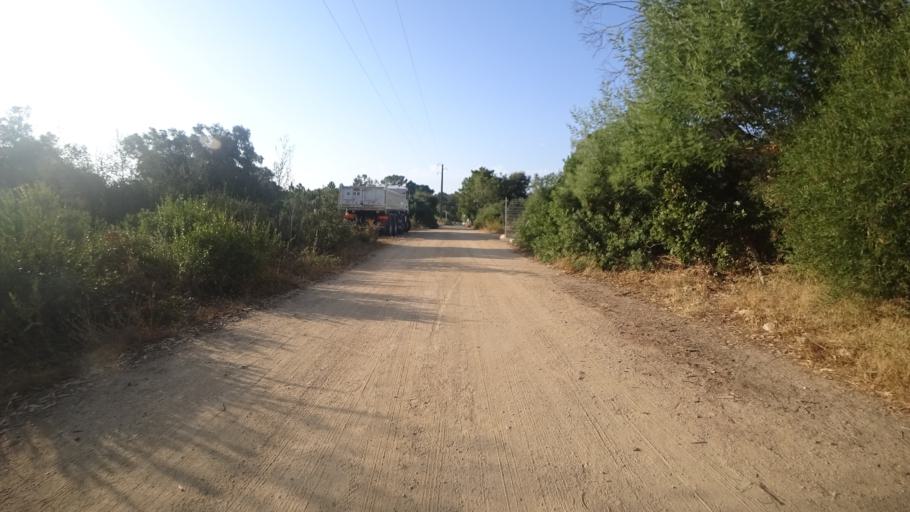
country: FR
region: Corsica
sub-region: Departement de la Corse-du-Sud
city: Porto-Vecchio
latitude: 41.6407
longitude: 9.3464
